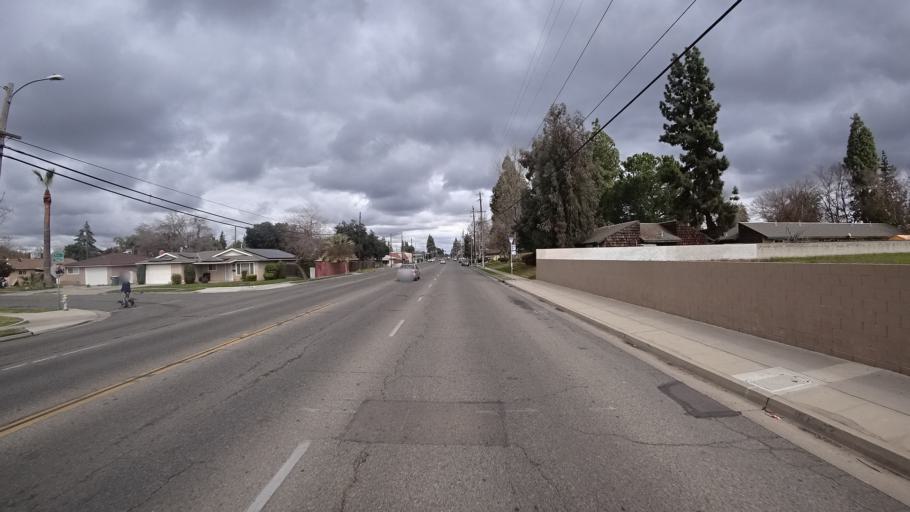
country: US
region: California
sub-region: Fresno County
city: West Park
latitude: 36.7914
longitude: -119.8443
